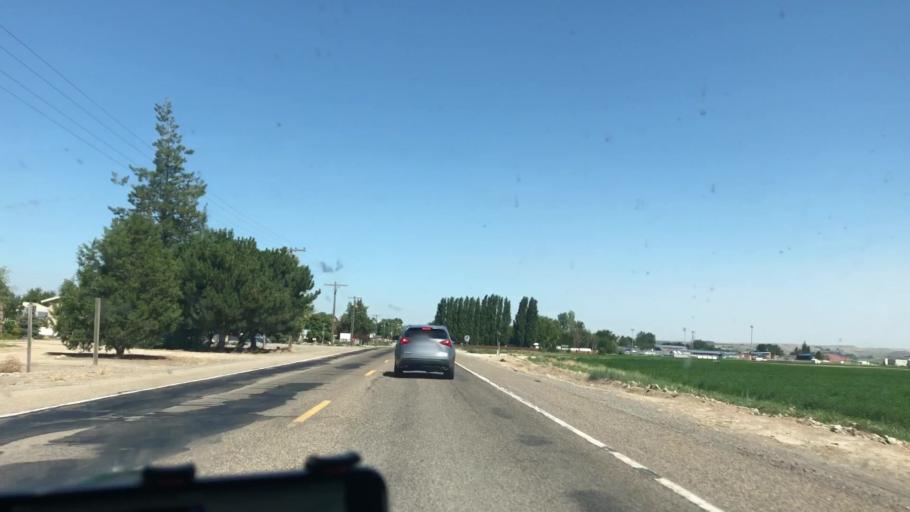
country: US
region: Idaho
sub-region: Owyhee County
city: Marsing
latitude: 43.5453
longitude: -116.8234
